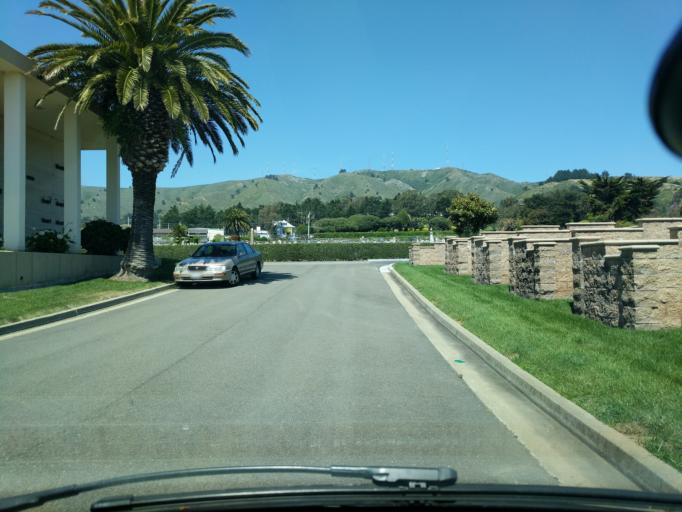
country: US
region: California
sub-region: San Mateo County
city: Colma
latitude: 37.6776
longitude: -122.4511
